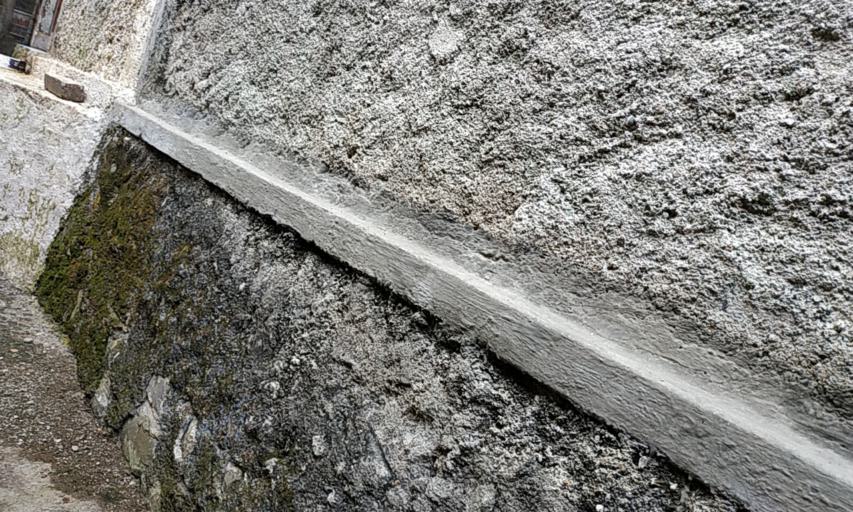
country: ID
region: Central Java
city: Gombong
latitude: -7.5849
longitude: 109.7150
